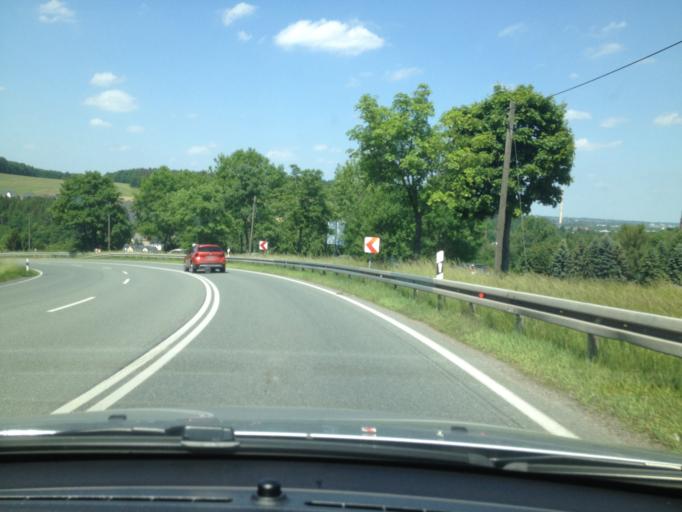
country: DE
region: Saxony
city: Burkhardtsdorf
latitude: 50.7715
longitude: 12.9279
